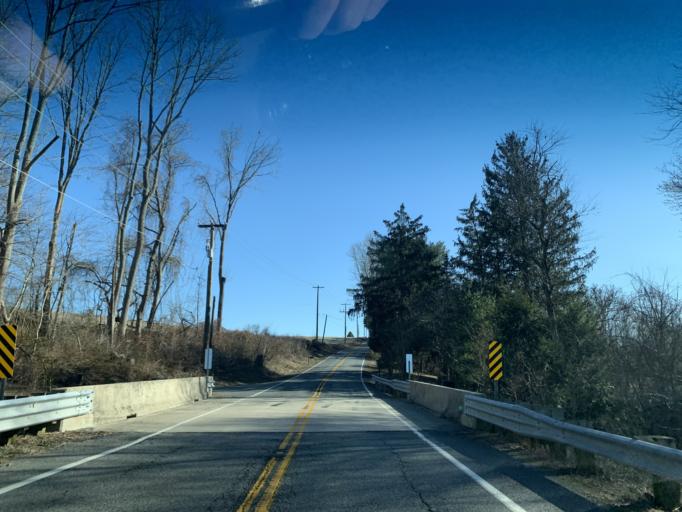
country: US
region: Maryland
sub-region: Cecil County
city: Rising Sun
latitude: 39.6584
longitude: -76.1036
